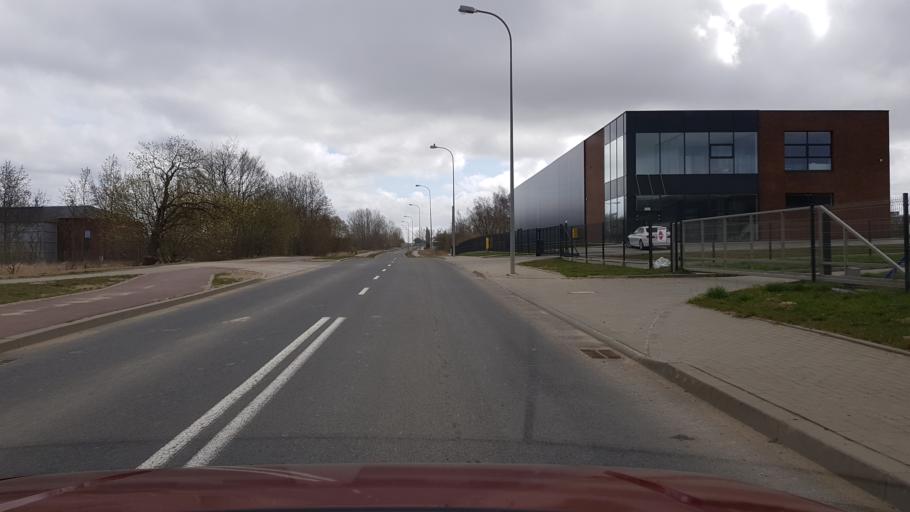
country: PL
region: West Pomeranian Voivodeship
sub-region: Koszalin
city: Koszalin
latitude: 54.1992
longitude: 16.1389
